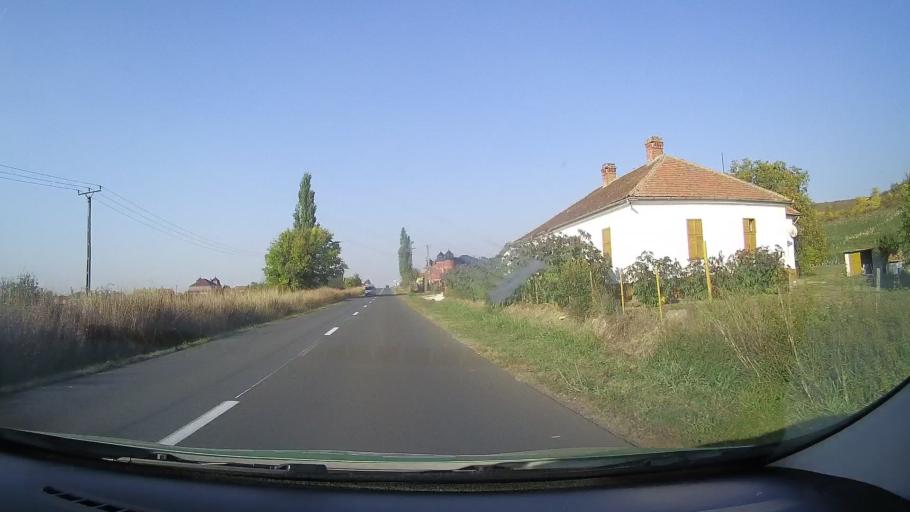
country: RO
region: Arad
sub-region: Comuna Covasint
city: Covasint
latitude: 46.1883
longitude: 21.6044
